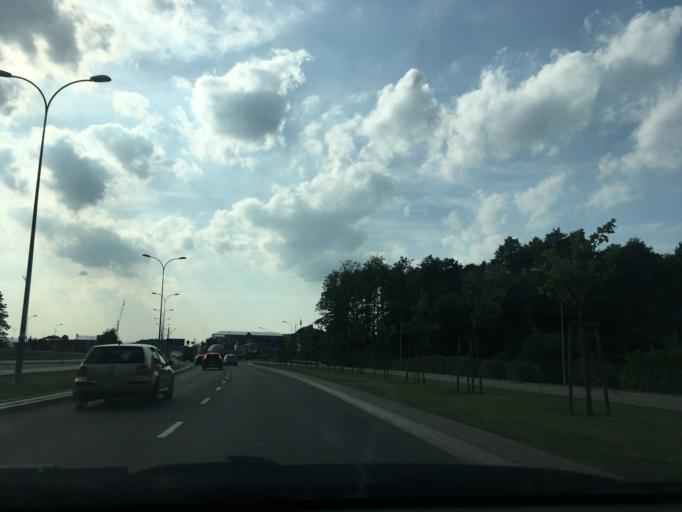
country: PL
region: Podlasie
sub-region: Bialystok
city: Bialystok
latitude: 53.1385
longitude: 23.2155
